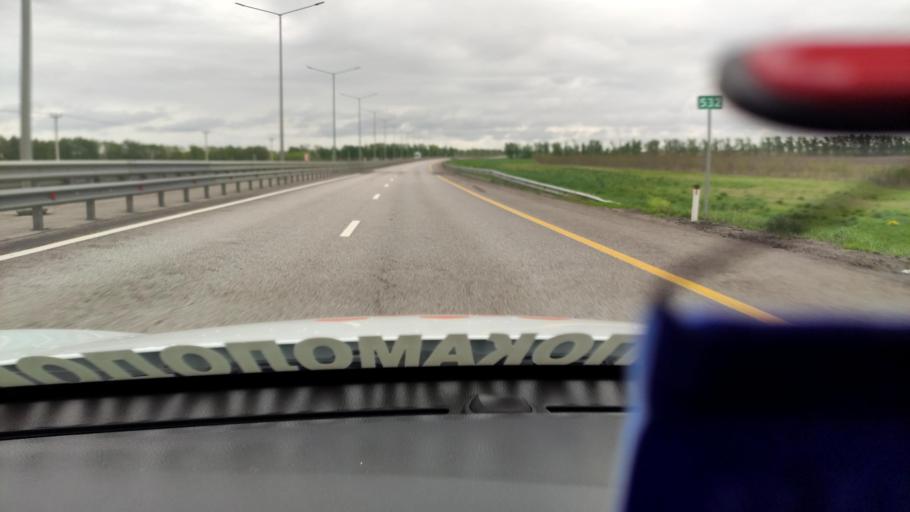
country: RU
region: Voronezj
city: Podkletnoye
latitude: 51.5841
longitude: 39.4563
